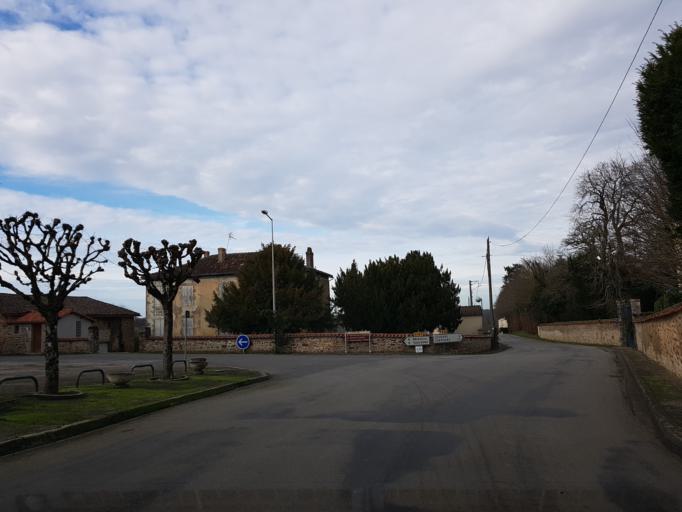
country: FR
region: Poitou-Charentes
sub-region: Departement de la Charente
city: Brigueuil
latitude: 46.0031
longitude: 0.8501
